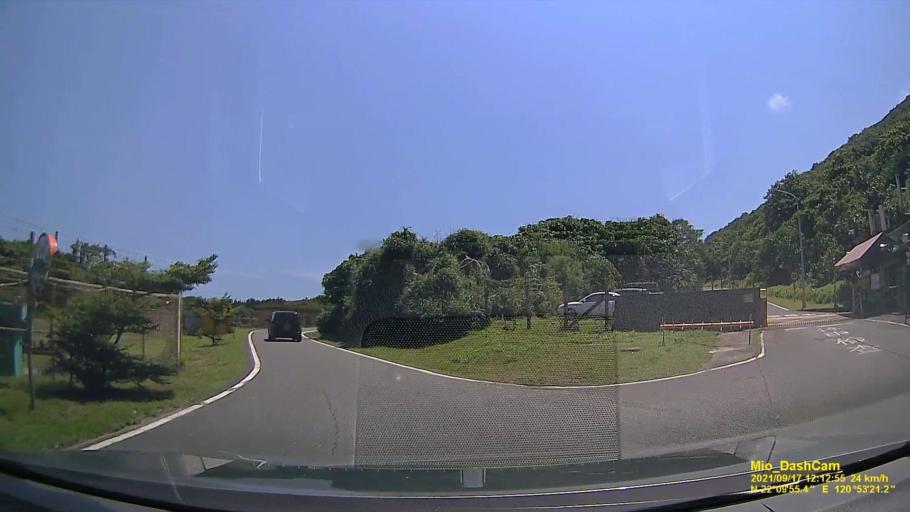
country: TW
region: Taiwan
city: Hengchun
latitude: 22.1654
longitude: 120.8892
